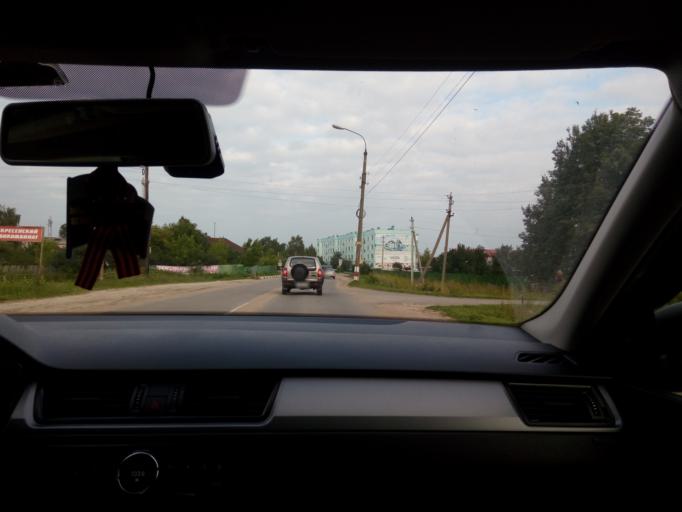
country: RU
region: Nizjnij Novgorod
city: Voskresenskoye
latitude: 56.8383
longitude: 45.4259
